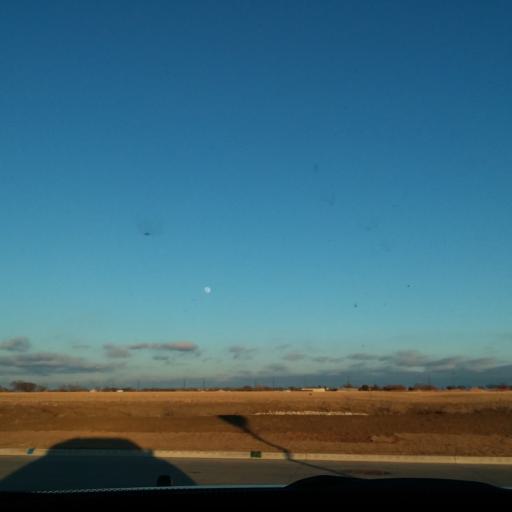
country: US
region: Texas
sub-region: Denton County
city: Krugerville
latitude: 33.2613
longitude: -96.8986
